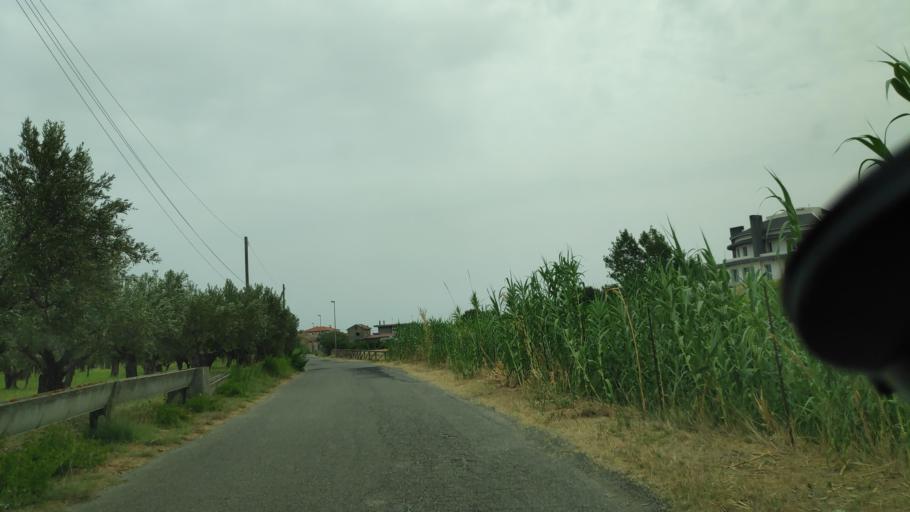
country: IT
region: Calabria
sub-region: Provincia di Catanzaro
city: Marina di Davoli
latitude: 38.6624
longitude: 16.5351
